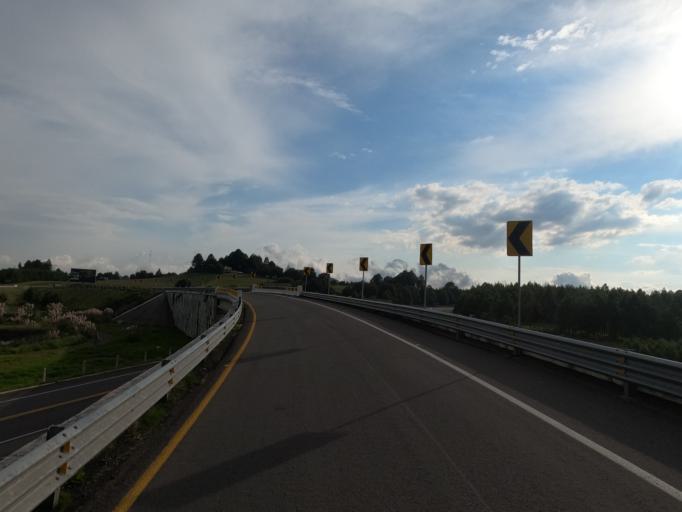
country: MX
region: Mexico
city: Amanalco de Becerra
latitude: 19.3539
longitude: -99.9867
